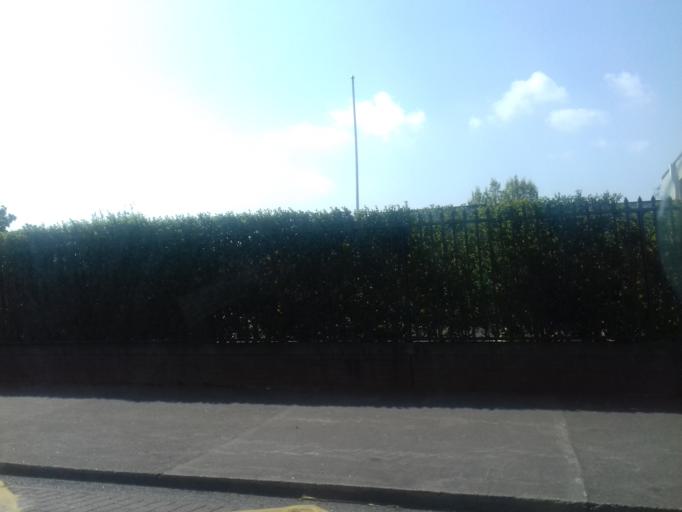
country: IE
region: Leinster
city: Raheny
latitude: 53.3928
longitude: -6.1722
